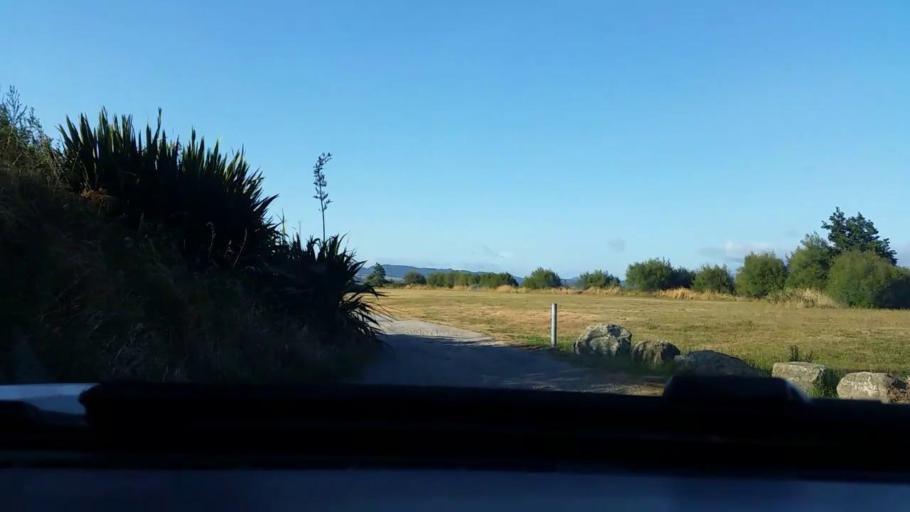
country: NZ
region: Bay of Plenty
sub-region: Rotorua District
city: Rotorua
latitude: -38.0797
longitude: 176.3223
